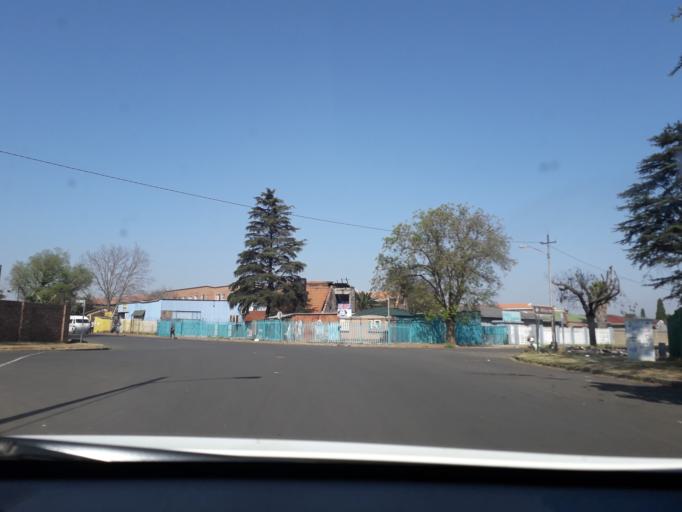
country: ZA
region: Gauteng
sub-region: City of Johannesburg Metropolitan Municipality
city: Modderfontein
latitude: -26.1014
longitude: 28.2392
